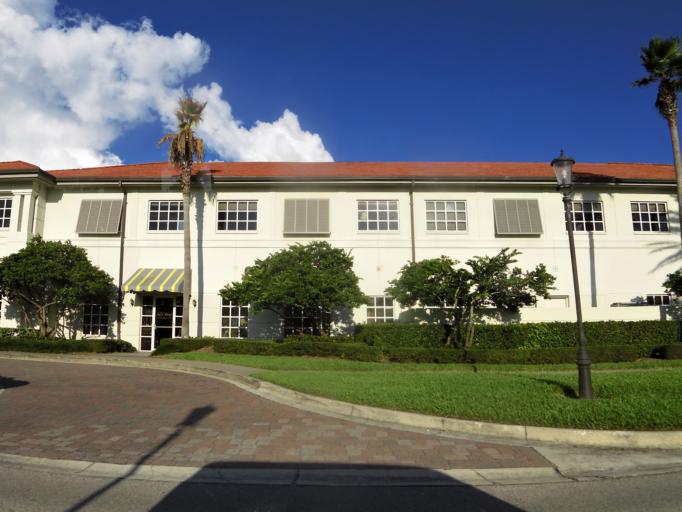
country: US
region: Florida
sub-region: Saint Johns County
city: Ponte Vedra Beach
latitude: 30.2398
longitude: -81.3781
